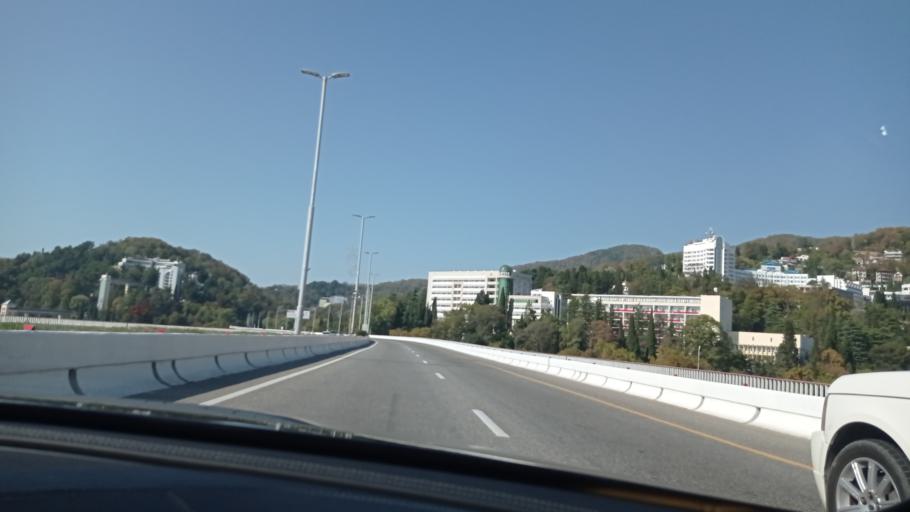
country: RU
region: Krasnodarskiy
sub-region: Sochi City
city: Khosta
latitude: 43.5107
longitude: 39.8659
